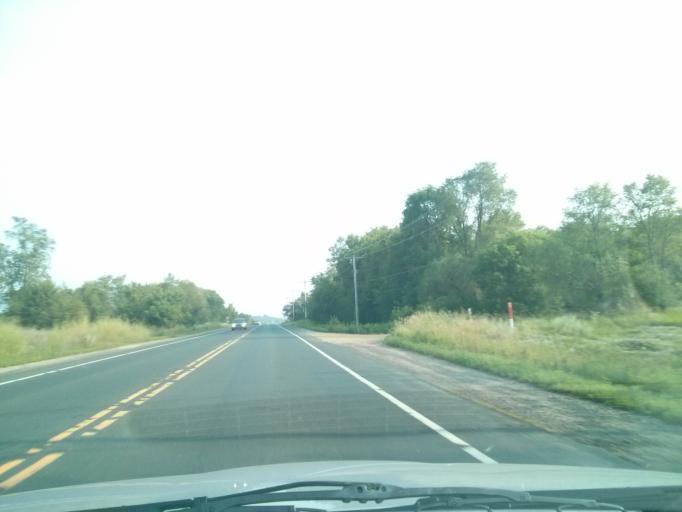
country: US
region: Wisconsin
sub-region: Saint Croix County
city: Hudson
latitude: 44.9730
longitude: -92.7211
